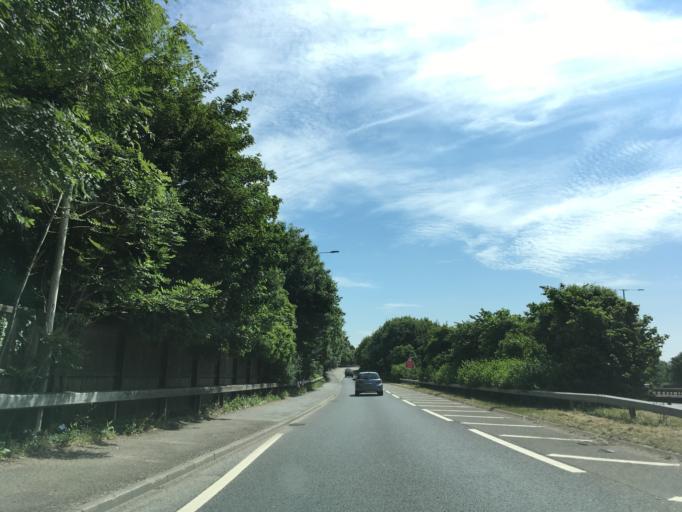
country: GB
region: England
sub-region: Greater London
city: Uxbridge
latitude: 51.5556
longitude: -0.4583
